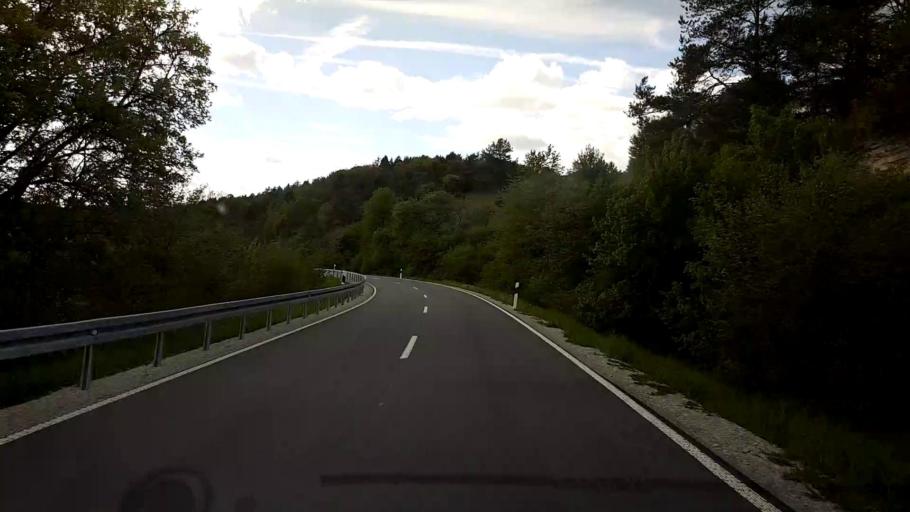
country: DE
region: Bavaria
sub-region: Upper Franconia
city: Hollfeld
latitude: 49.9517
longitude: 11.2768
